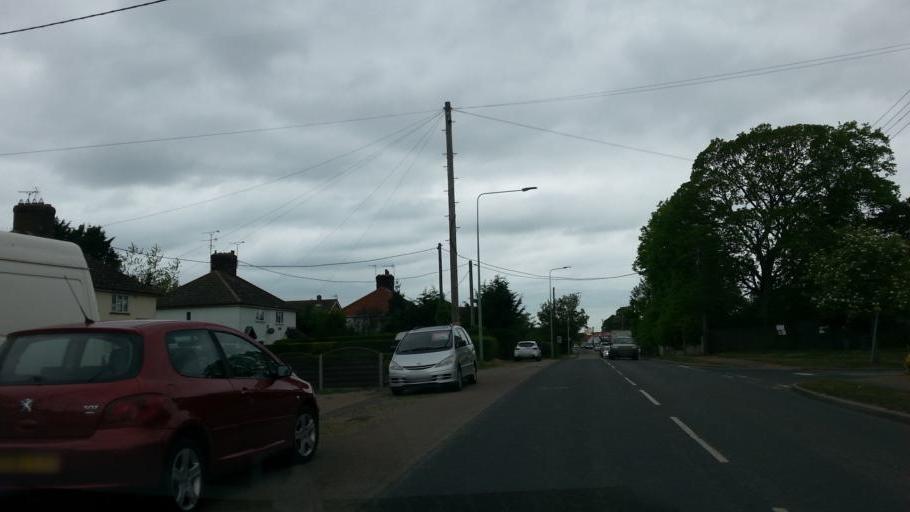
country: GB
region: England
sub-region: Suffolk
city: Lakenheath
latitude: 52.3674
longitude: 0.4879
